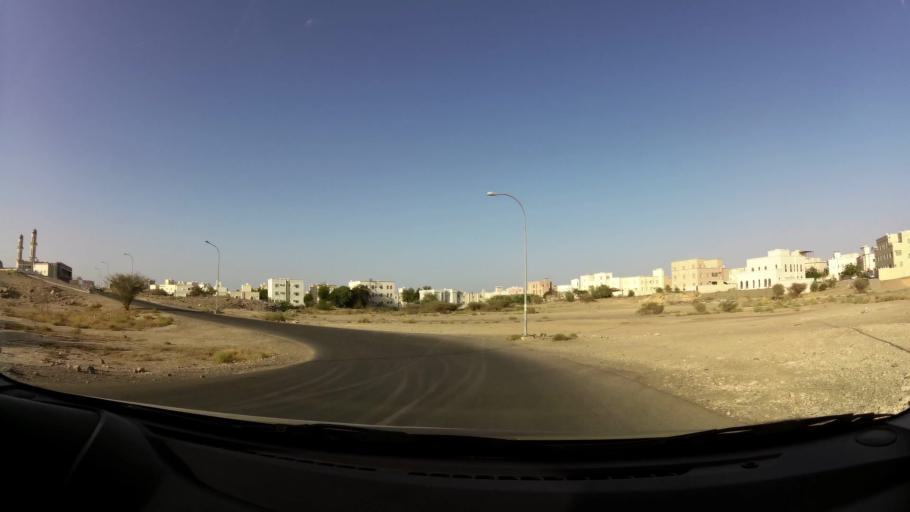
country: OM
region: Muhafazat Masqat
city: As Sib al Jadidah
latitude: 23.6055
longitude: 58.2176
